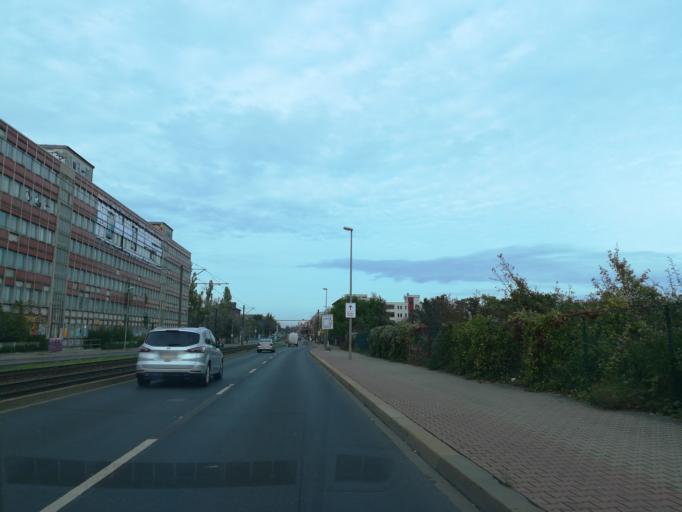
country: DE
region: Saxony-Anhalt
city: Magdeburg
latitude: 52.1212
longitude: 11.6068
